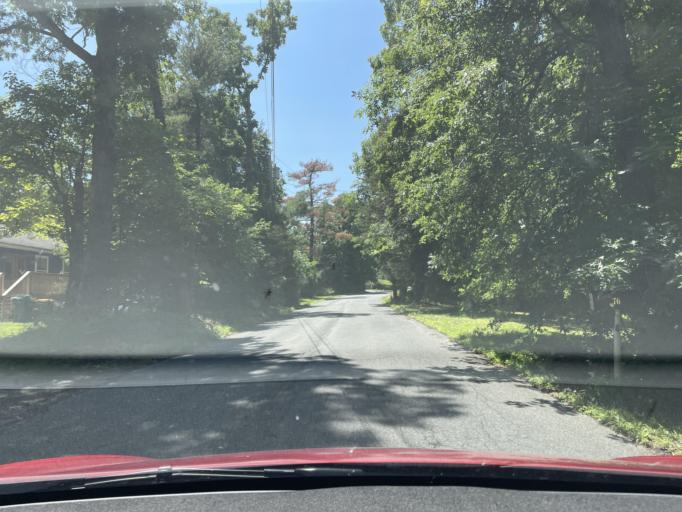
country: US
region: New York
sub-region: Ulster County
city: Lake Katrine
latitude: 42.0163
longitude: -73.9764
